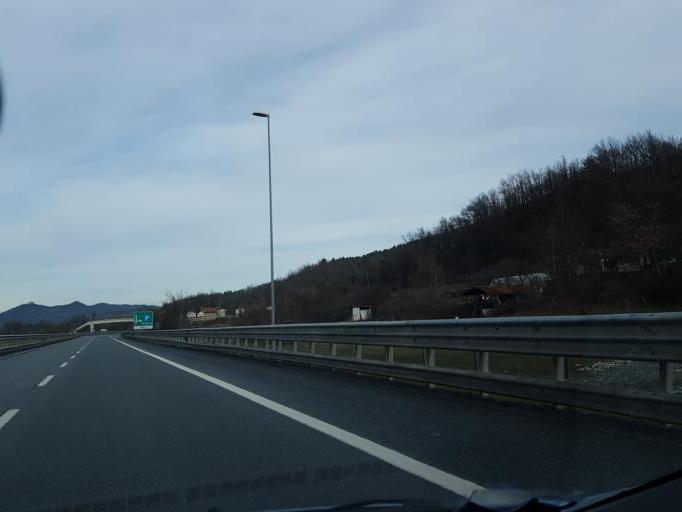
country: IT
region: Piedmont
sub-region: Provincia di Alessandria
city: Arquata Scrivia
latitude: 44.6724
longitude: 8.9057
